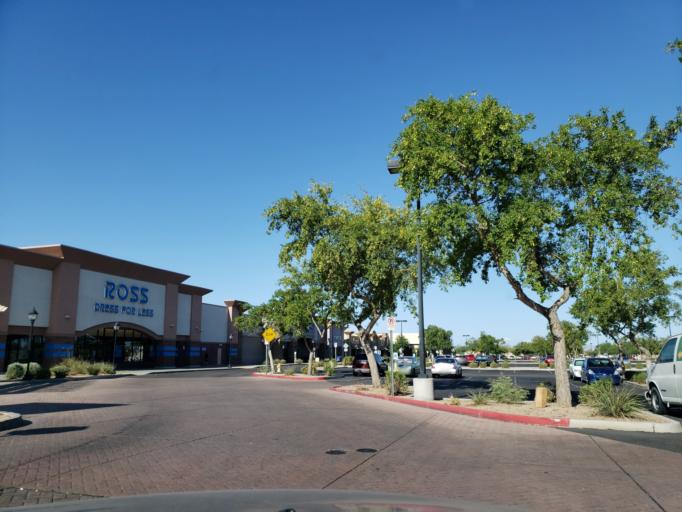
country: US
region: Arizona
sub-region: Maricopa County
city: Glendale
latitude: 33.5518
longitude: -112.1814
